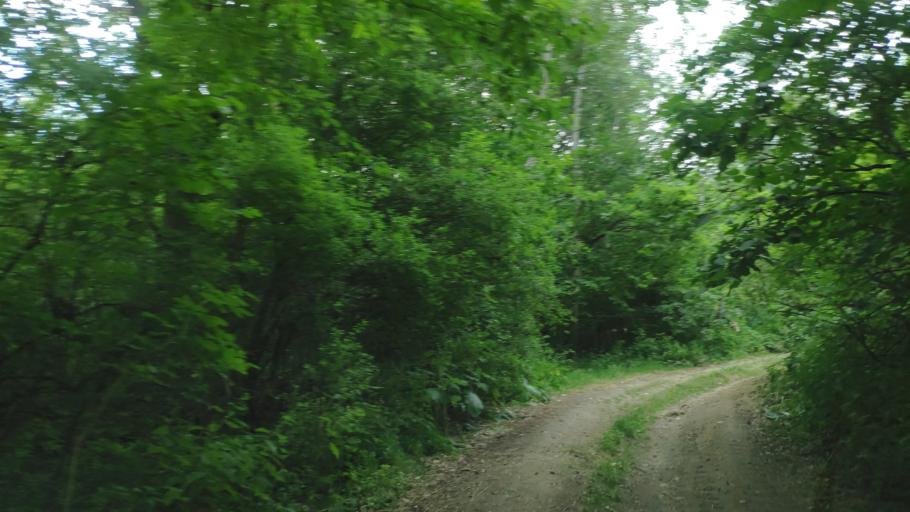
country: SK
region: Kosicky
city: Moldava nad Bodvou
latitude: 48.7077
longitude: 20.9907
